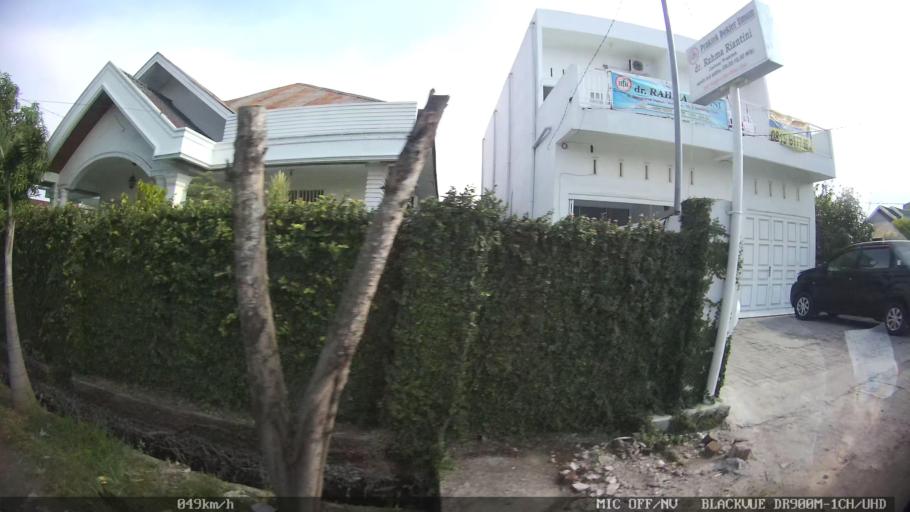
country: ID
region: North Sumatra
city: Percut
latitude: 3.5940
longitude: 98.7692
